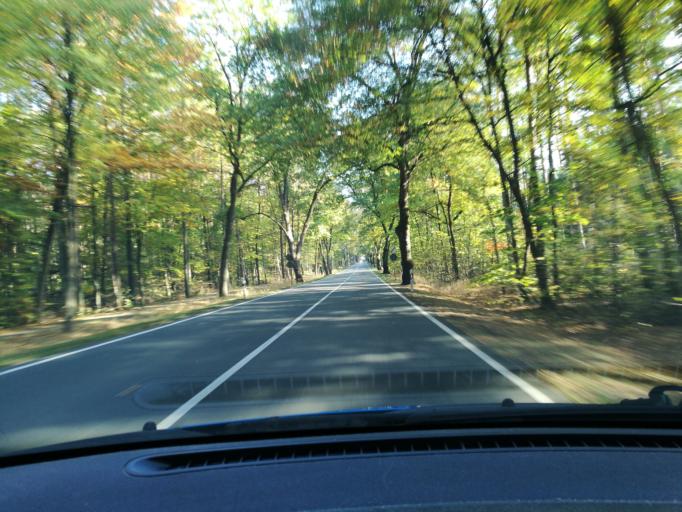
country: DE
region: Lower Saxony
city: Karwitz
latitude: 53.1144
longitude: 11.0086
